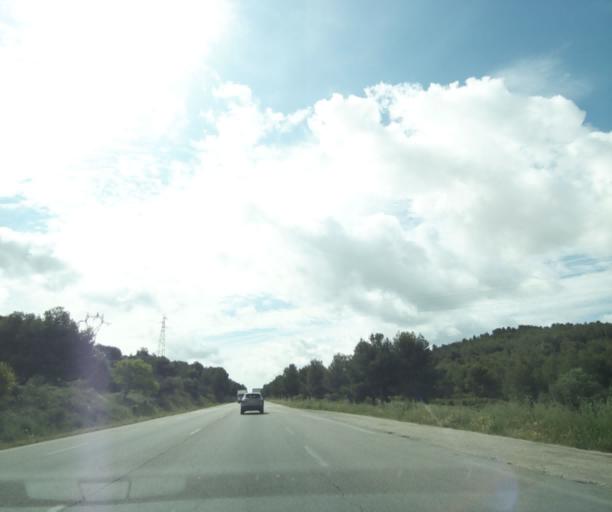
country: FR
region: Provence-Alpes-Cote d'Azur
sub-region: Departement des Bouches-du-Rhone
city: La Fare-les-Oliviers
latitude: 43.5152
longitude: 5.2021
